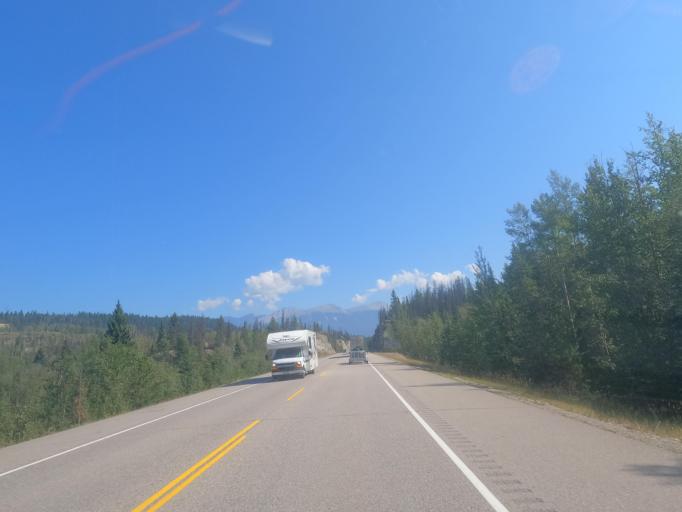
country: CA
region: Alberta
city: Jasper Park Lodge
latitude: 52.8605
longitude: -118.1120
